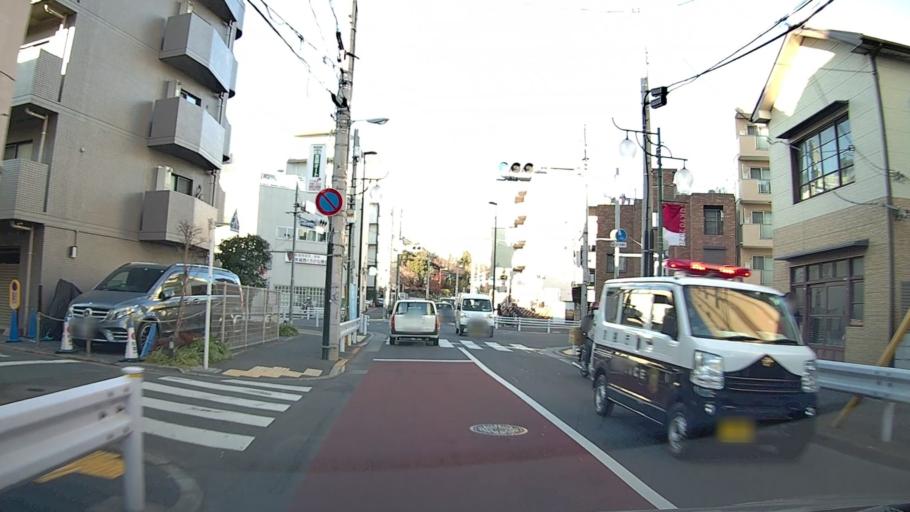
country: JP
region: Tokyo
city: Tokyo
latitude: 35.7021
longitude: 139.6721
